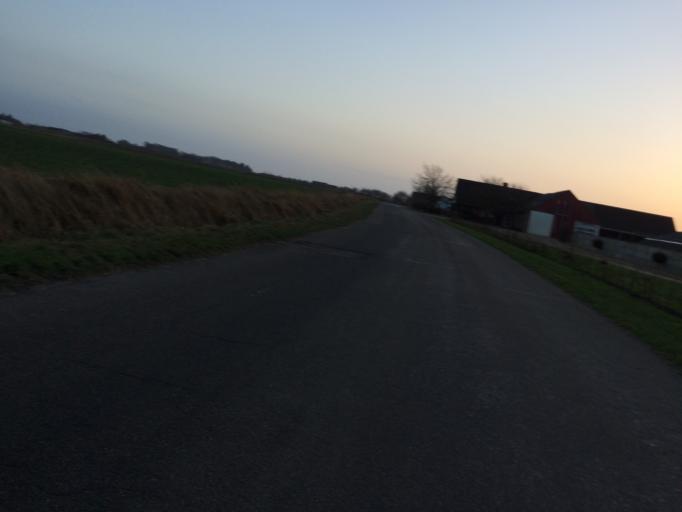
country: DK
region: Central Jutland
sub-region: Holstebro Kommune
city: Ulfborg
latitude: 56.2821
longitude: 8.2864
